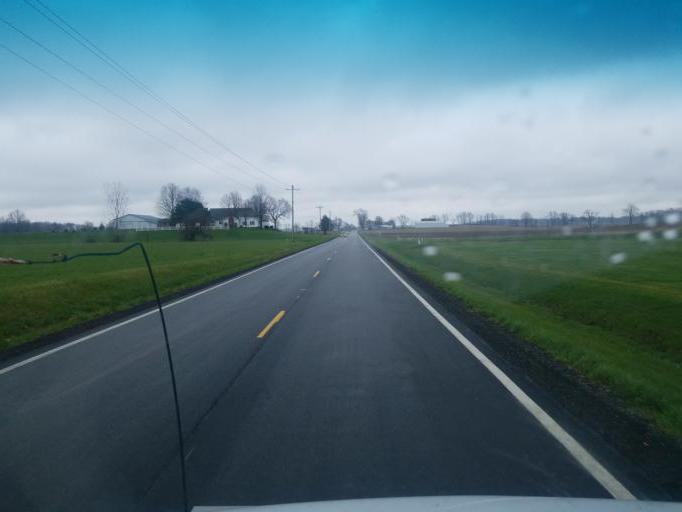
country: US
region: Ohio
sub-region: Huron County
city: Willard
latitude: 40.9601
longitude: -82.7863
